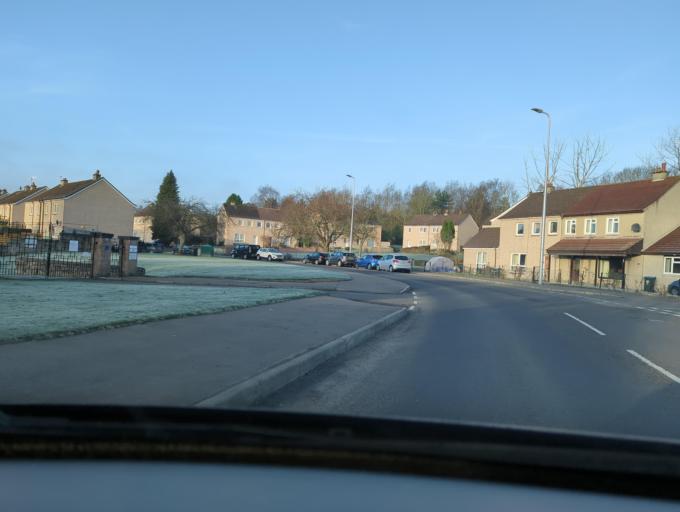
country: GB
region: Scotland
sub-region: Perth and Kinross
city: Perth
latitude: 56.4030
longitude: -3.4524
